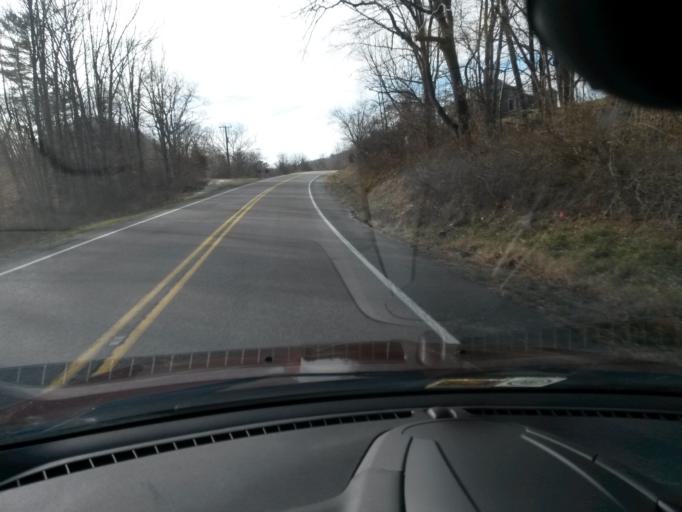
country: US
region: Virginia
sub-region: Augusta County
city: Jolivue
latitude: 38.1126
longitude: -79.2988
